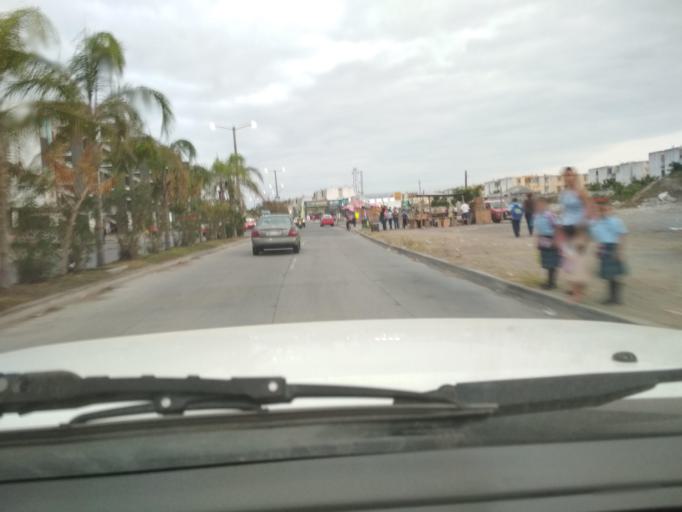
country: MX
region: Veracruz
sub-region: Medellin
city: Fraccionamiento Arboledas San Ramon
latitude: 19.0940
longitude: -96.1641
